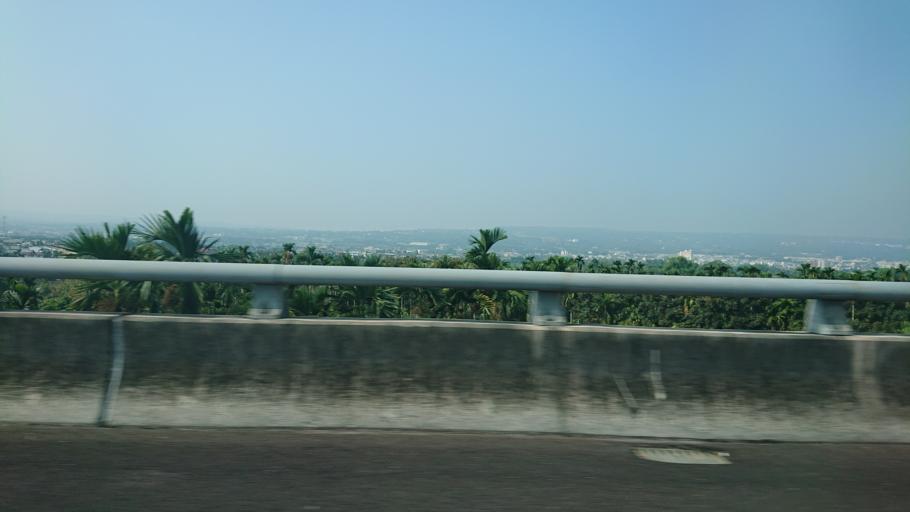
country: TW
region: Taiwan
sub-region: Nantou
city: Nantou
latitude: 23.8962
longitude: 120.7106
